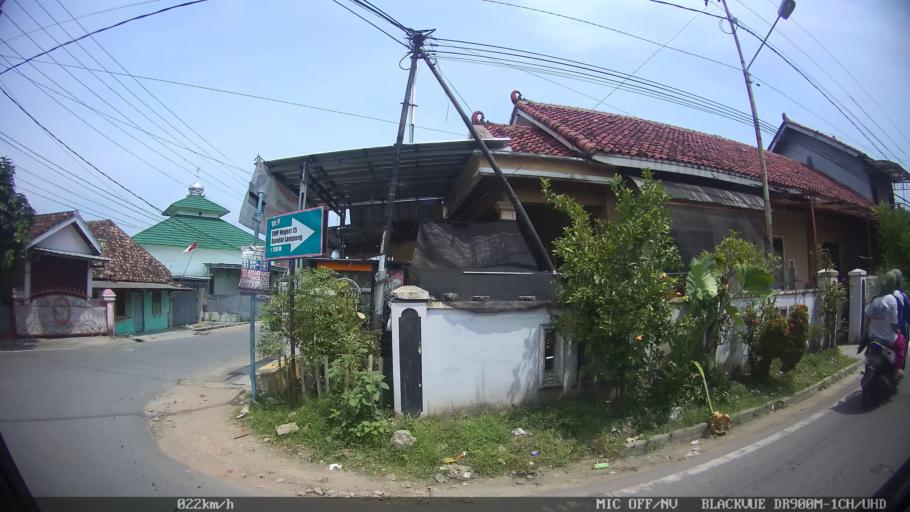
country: ID
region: Lampung
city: Bandarlampung
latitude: -5.4517
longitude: 105.2560
